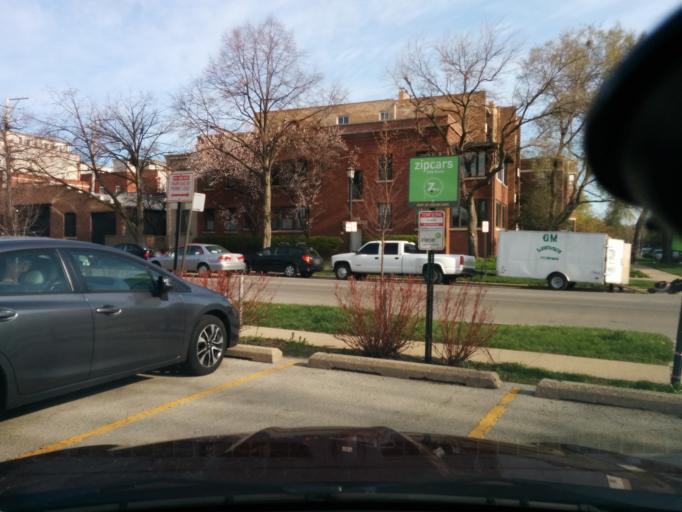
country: US
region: Illinois
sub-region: Cook County
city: Evanston
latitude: 42.0271
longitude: -87.6767
